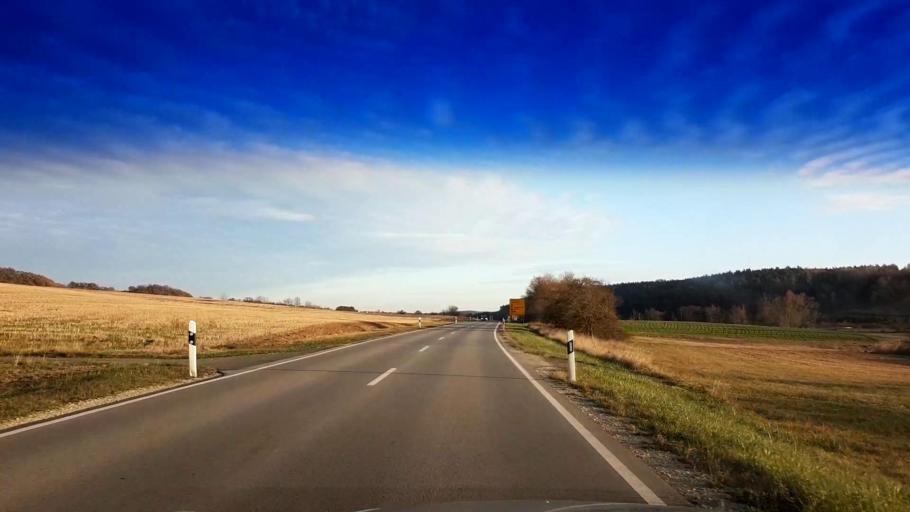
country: DE
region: Bavaria
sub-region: Upper Franconia
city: Priesendorf
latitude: 49.8925
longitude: 10.7343
